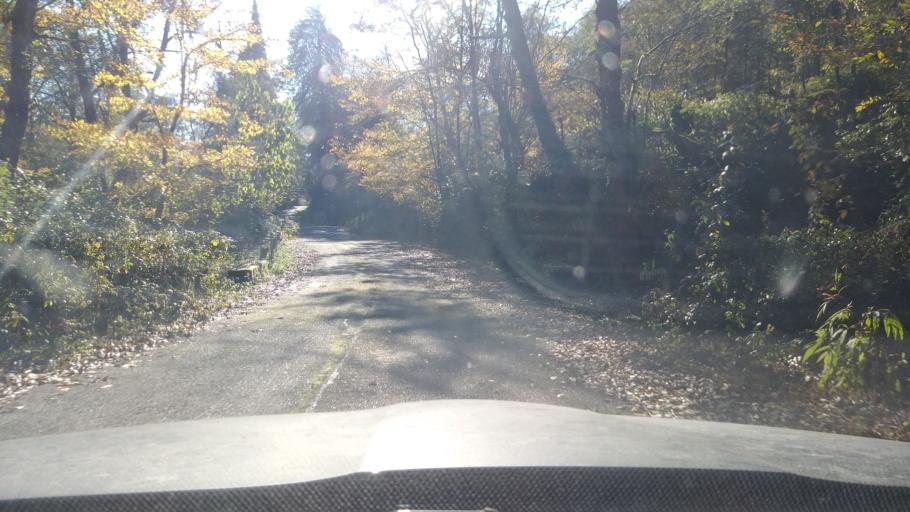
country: GE
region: Abkhazia
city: Bich'vinta
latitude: 43.1856
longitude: 40.4538
